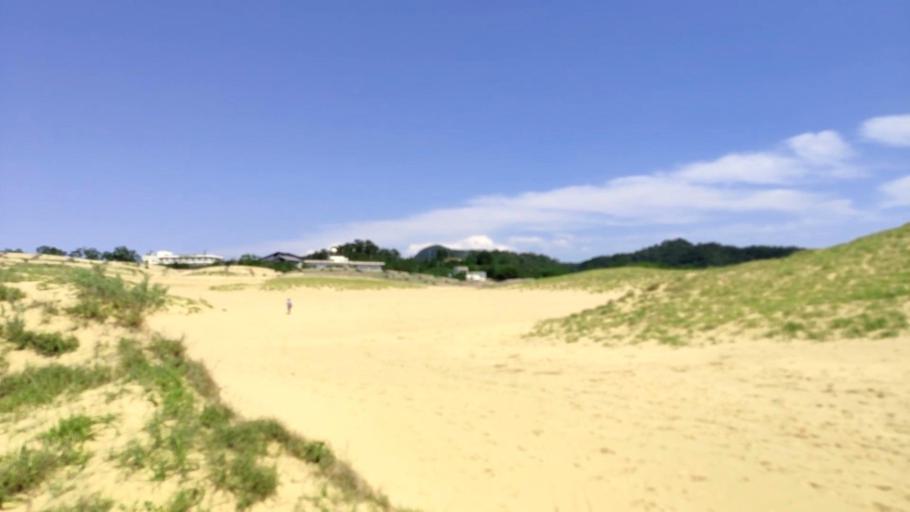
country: JP
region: Tottori
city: Tottori
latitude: 35.5418
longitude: 134.2332
